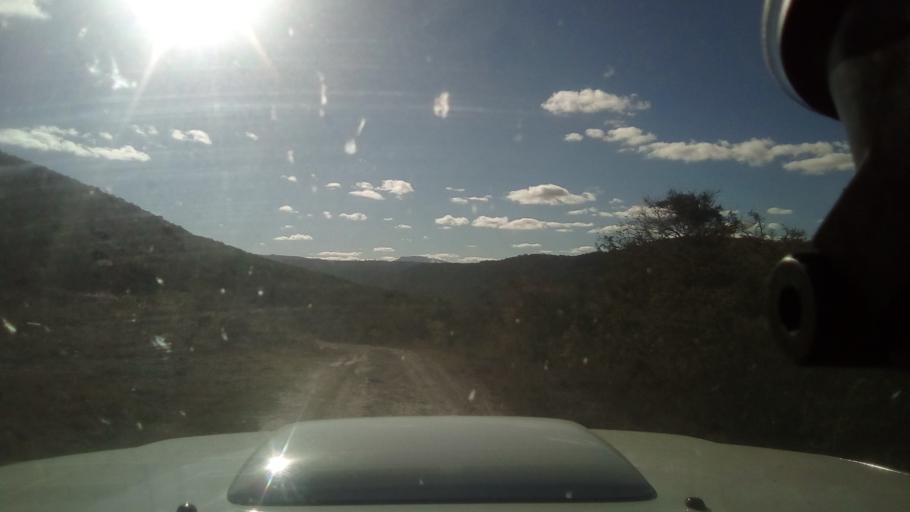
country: ZA
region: Eastern Cape
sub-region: Buffalo City Metropolitan Municipality
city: Bhisho
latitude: -32.7371
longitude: 27.3482
